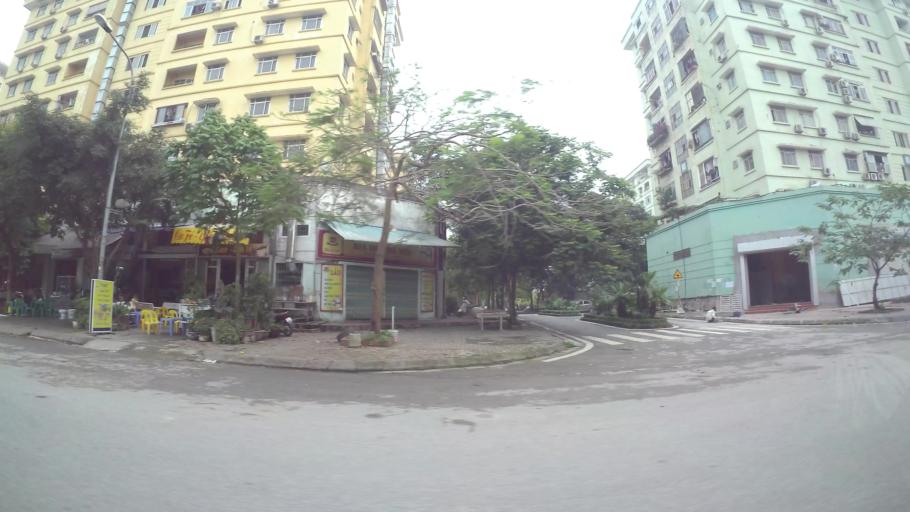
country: VN
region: Ha Noi
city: Van Dien
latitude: 20.9703
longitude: 105.8474
